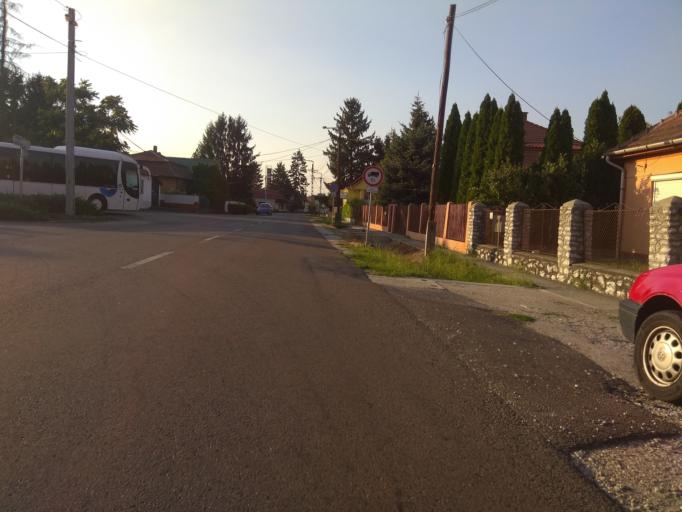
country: HU
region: Borsod-Abauj-Zemplen
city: Nyekladhaza
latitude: 47.9904
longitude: 20.8372
